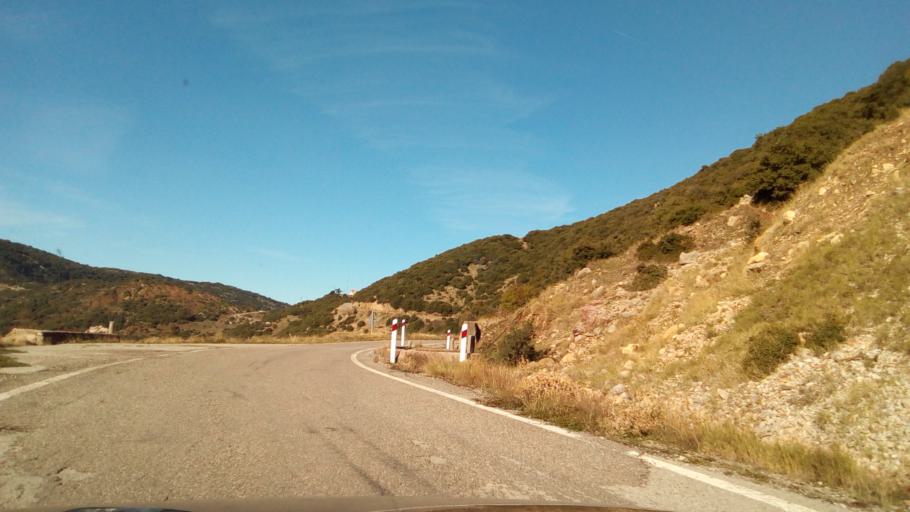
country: GR
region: West Greece
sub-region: Nomos Aitolias kai Akarnanias
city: Nafpaktos
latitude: 38.5012
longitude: 21.8466
